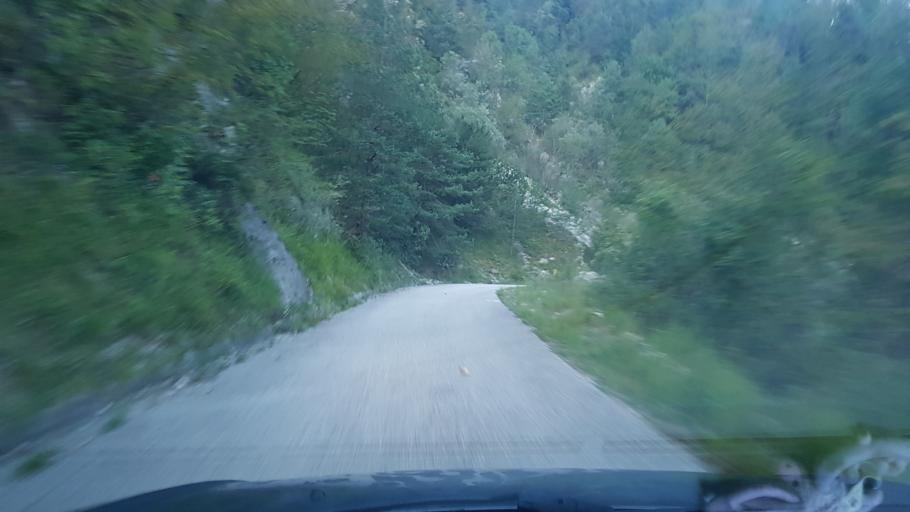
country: IT
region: Friuli Venezia Giulia
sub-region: Provincia di Pordenone
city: Frisanco
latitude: 46.2601
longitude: 12.7024
